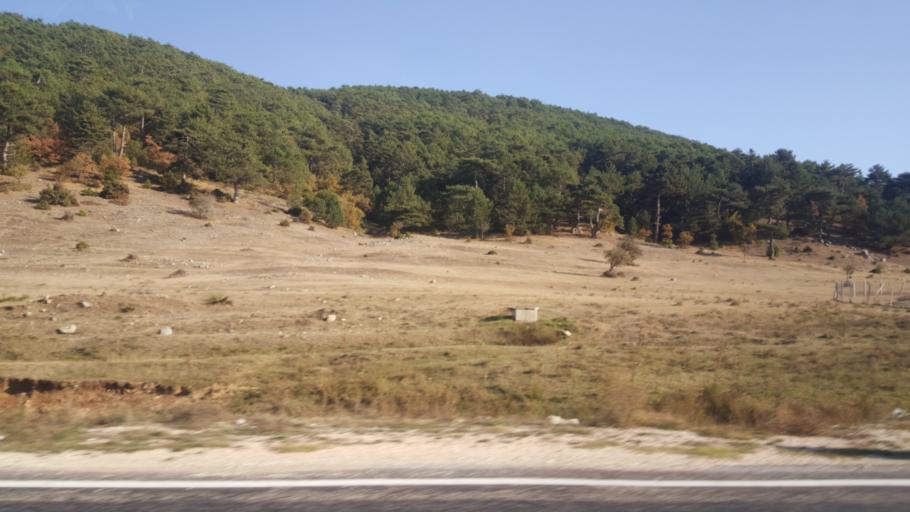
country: TR
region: Afyonkarahisar
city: Ihsaniye
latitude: 39.1018
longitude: 30.5796
